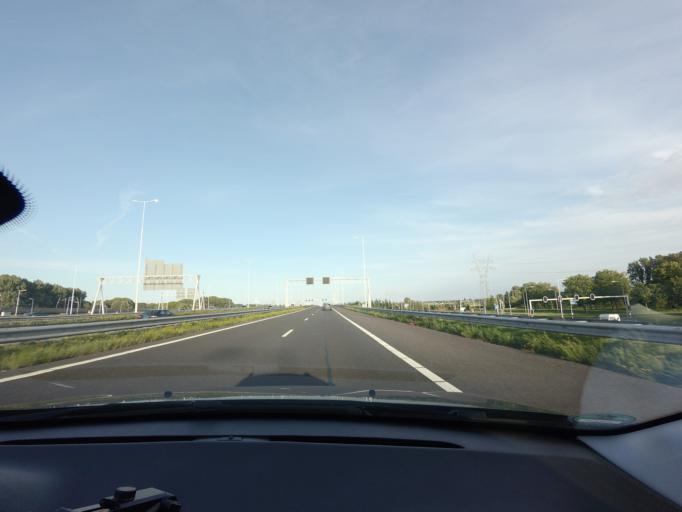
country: NL
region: South Holland
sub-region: Gemeente Albrandswaard
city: Rhoon
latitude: 51.8679
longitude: 4.4402
